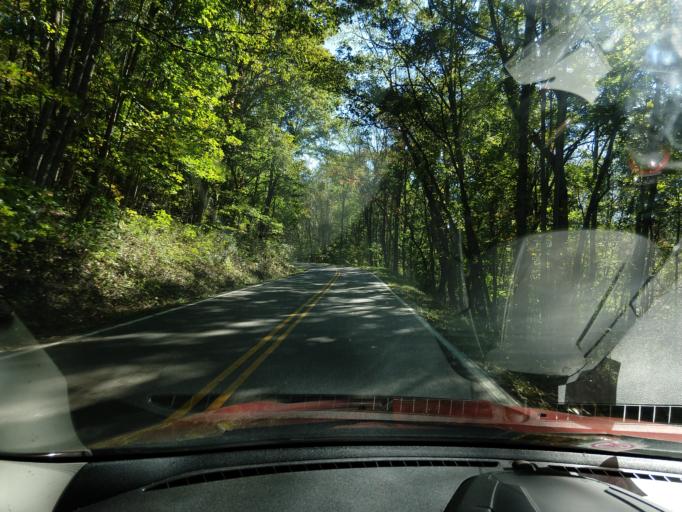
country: US
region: Virginia
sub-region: Alleghany County
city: Clifton Forge
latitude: 37.8881
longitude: -79.8865
